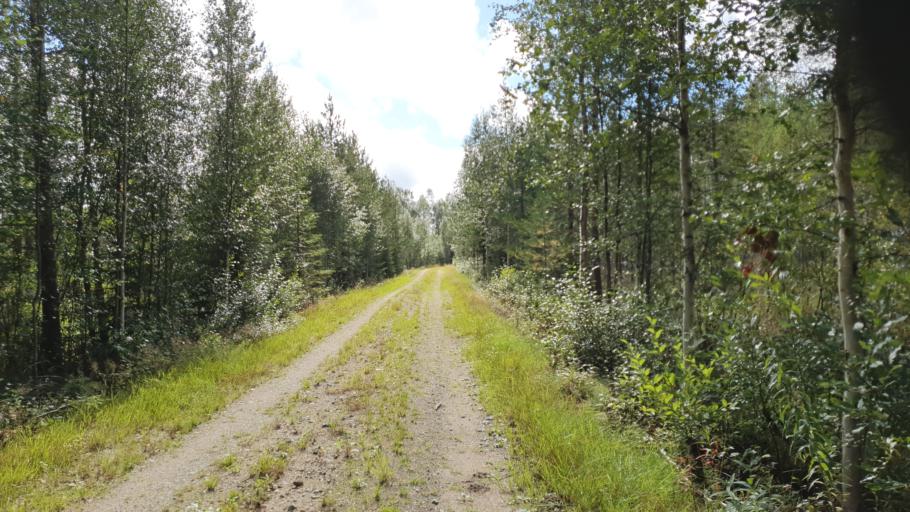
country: FI
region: Kainuu
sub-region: Kehys-Kainuu
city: Kuhmo
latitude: 64.1477
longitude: 29.3555
